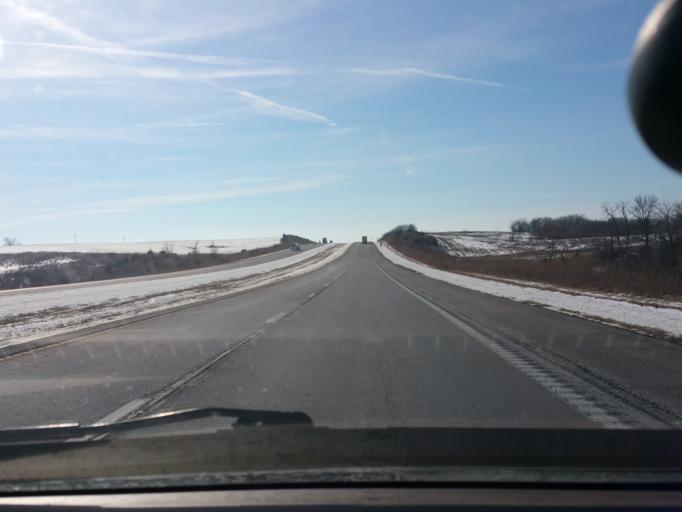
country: US
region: Iowa
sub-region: Decatur County
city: Lamoni
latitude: 40.5041
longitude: -93.9665
